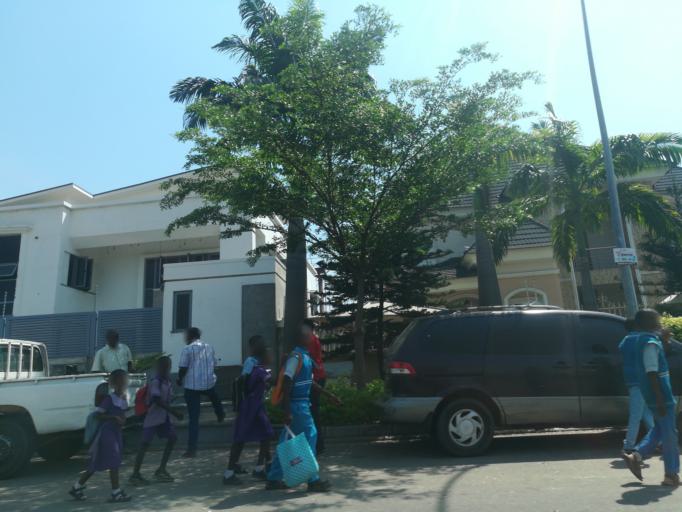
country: NG
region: Abuja Federal Capital Territory
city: Abuja
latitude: 9.0661
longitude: 7.4264
